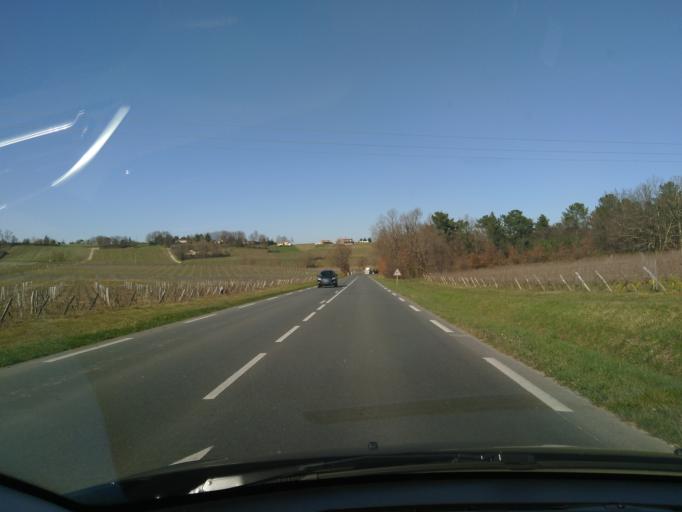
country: FR
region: Aquitaine
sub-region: Departement de la Dordogne
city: Monbazillac
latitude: 44.7836
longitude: 0.5255
